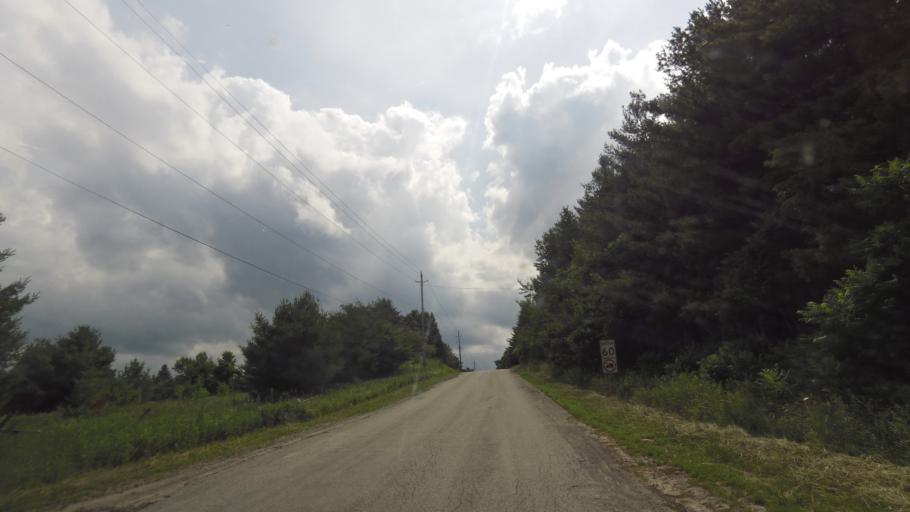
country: CA
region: Ontario
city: Orangeville
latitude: 43.8791
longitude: -79.9257
